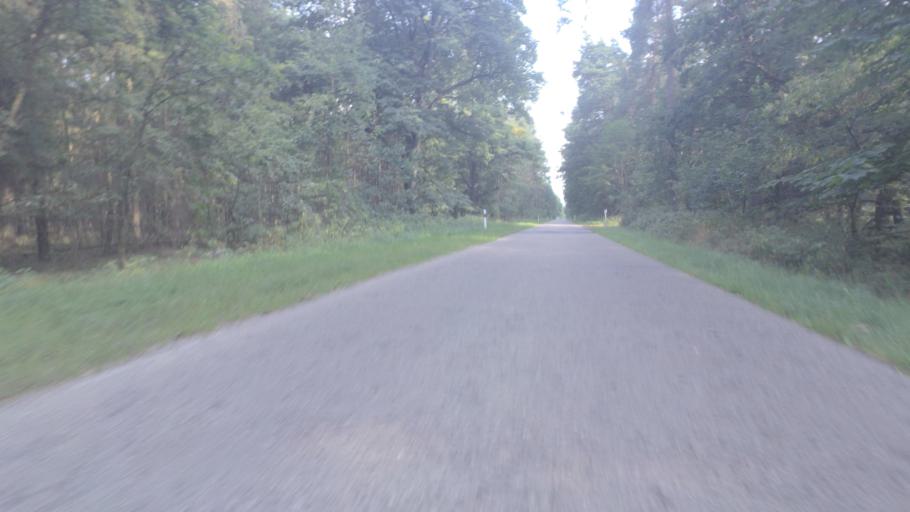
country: DE
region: Brandenburg
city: Wittstock
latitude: 53.2647
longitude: 12.4593
